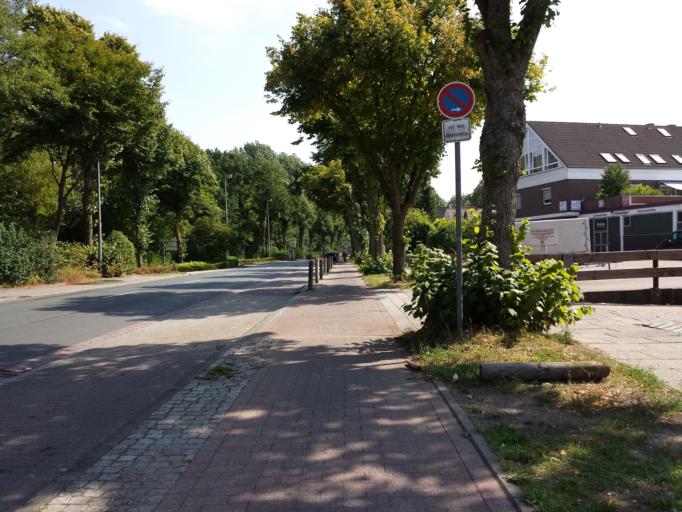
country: DE
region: Bremen
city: Bremen
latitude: 53.0397
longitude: 8.8335
